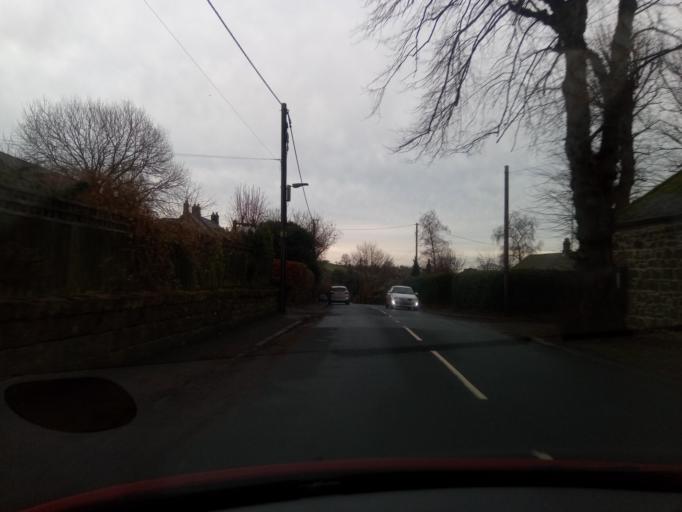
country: GB
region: England
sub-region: Northumberland
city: Whittingham
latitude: 55.4697
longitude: -1.8341
